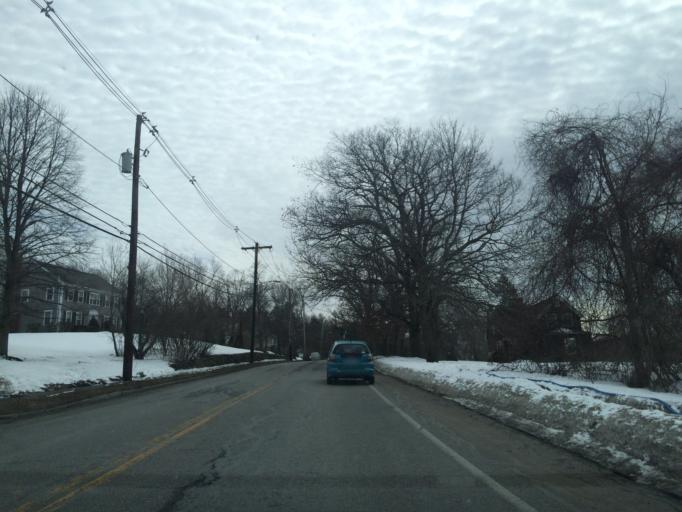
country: US
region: Massachusetts
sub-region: Middlesex County
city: Lexington
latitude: 42.4294
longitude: -71.2316
